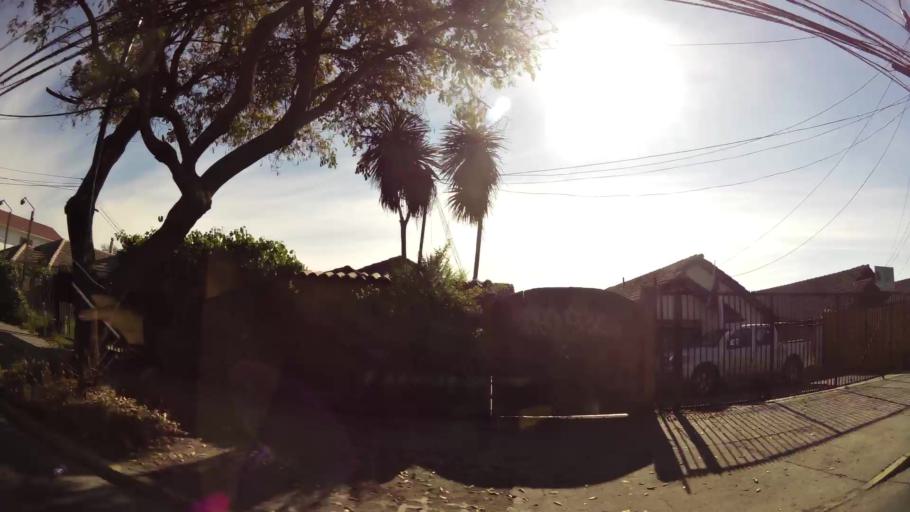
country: CL
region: Santiago Metropolitan
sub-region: Provincia de Santiago
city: Villa Presidente Frei, Nunoa, Santiago, Chile
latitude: -33.5012
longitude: -70.5610
